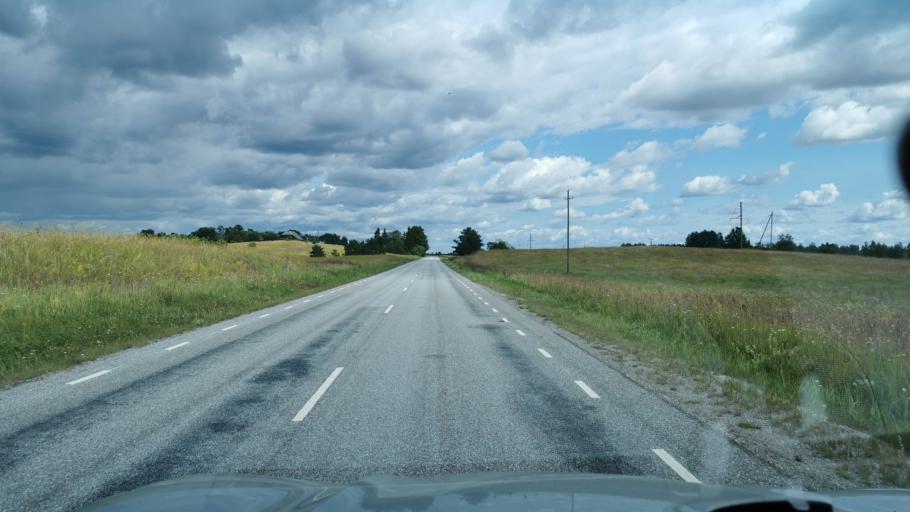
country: EE
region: Harju
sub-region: Kuusalu vald
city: Kuusalu
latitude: 59.2143
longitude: 25.6030
